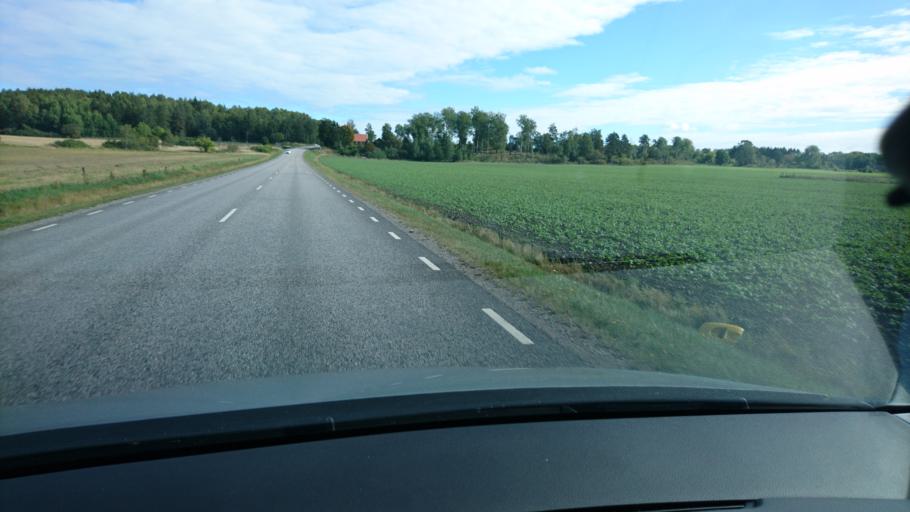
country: SE
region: Soedermanland
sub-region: Strangnas Kommun
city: Strangnas
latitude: 59.3365
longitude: 17.0796
